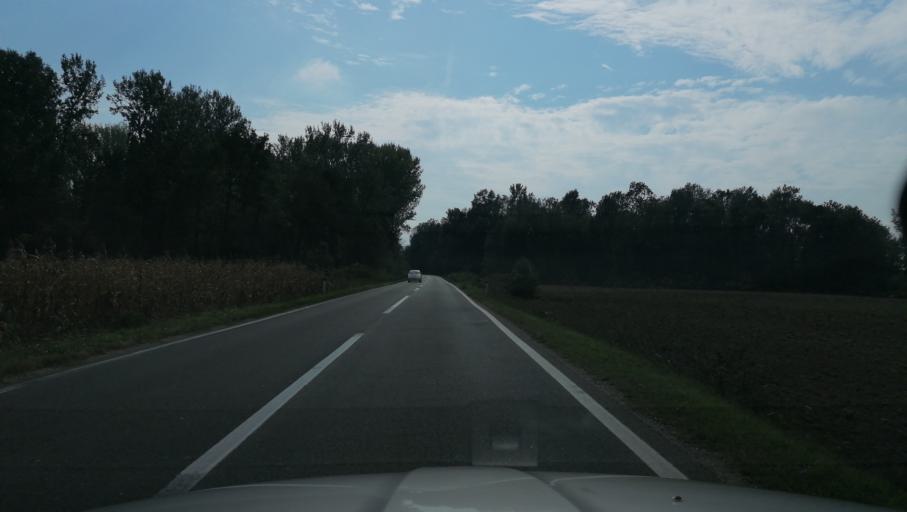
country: BA
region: Republika Srpska
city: Balatun
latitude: 44.8809
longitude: 19.3317
